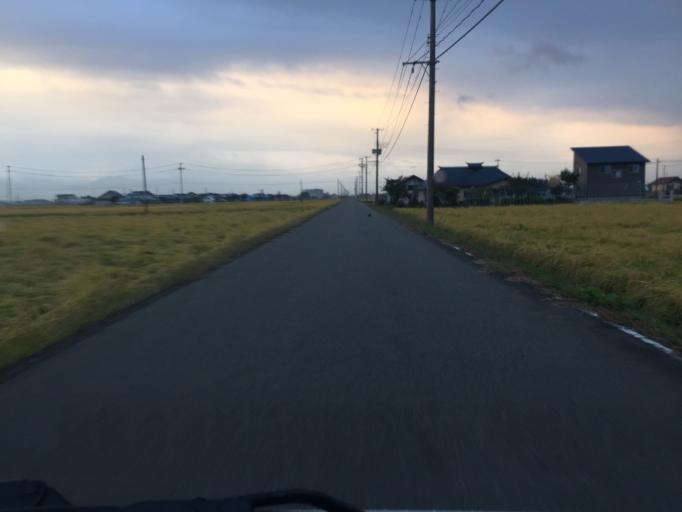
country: JP
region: Fukushima
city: Kitakata
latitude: 37.5696
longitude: 139.9069
